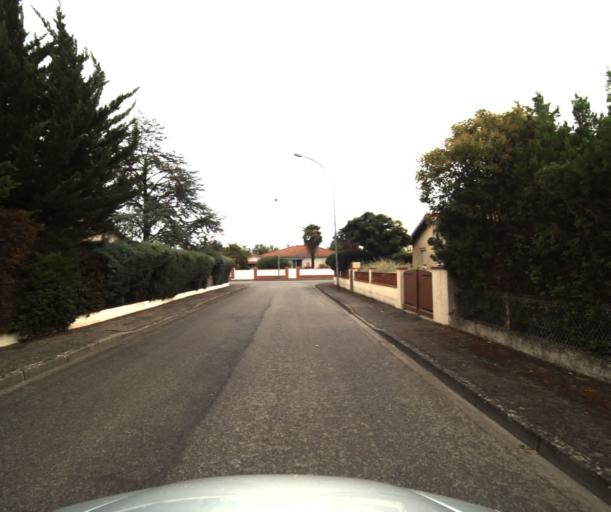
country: FR
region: Midi-Pyrenees
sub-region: Departement de la Haute-Garonne
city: Muret
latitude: 43.4663
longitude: 1.3354
